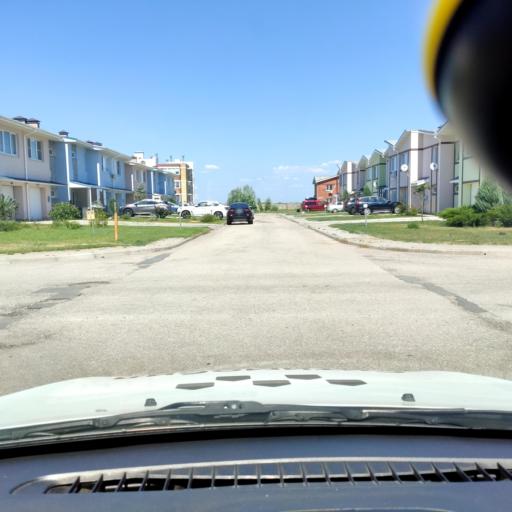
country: RU
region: Samara
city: Tol'yatti
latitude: 53.6185
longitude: 49.3172
